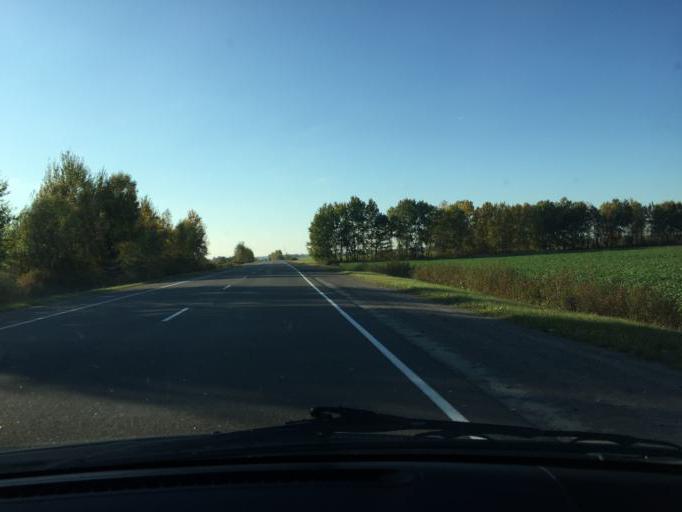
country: BY
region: Brest
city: Horad Luninyets
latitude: 52.3102
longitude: 26.6720
